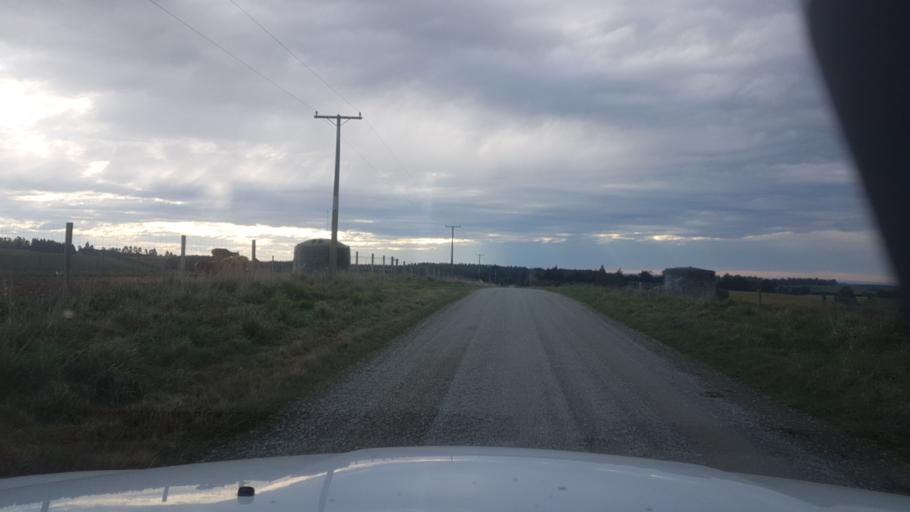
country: NZ
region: Canterbury
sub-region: Timaru District
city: Pleasant Point
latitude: -44.3365
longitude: 171.1502
